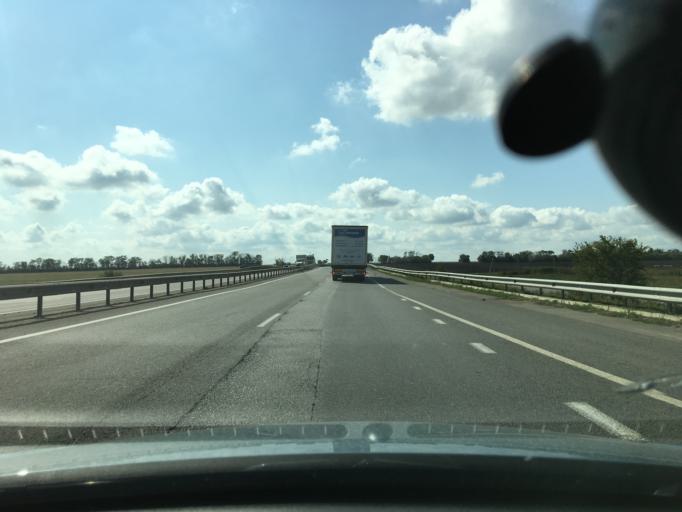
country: RU
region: Krasnodarskiy
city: Krasnoye
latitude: 46.7320
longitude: 39.6562
